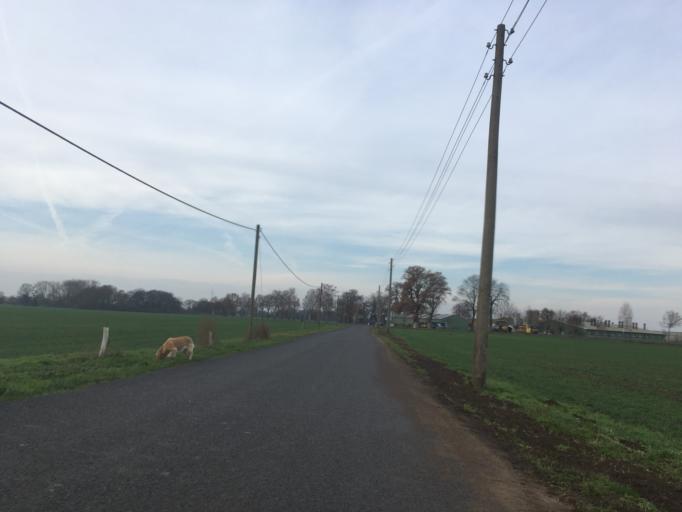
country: DE
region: Brandenburg
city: Neulewin
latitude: 52.7109
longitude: 14.3185
